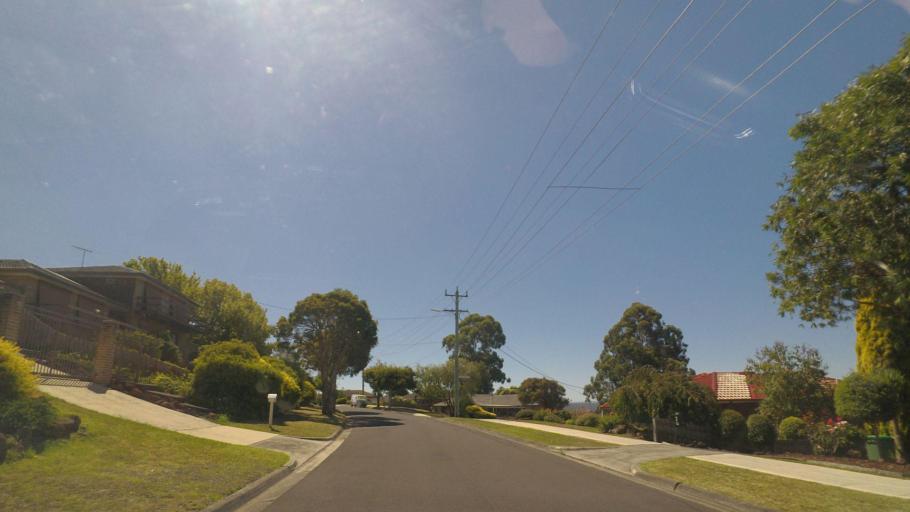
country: AU
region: Victoria
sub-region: Yarra Ranges
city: Lilydale
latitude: -37.7538
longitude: 145.3340
